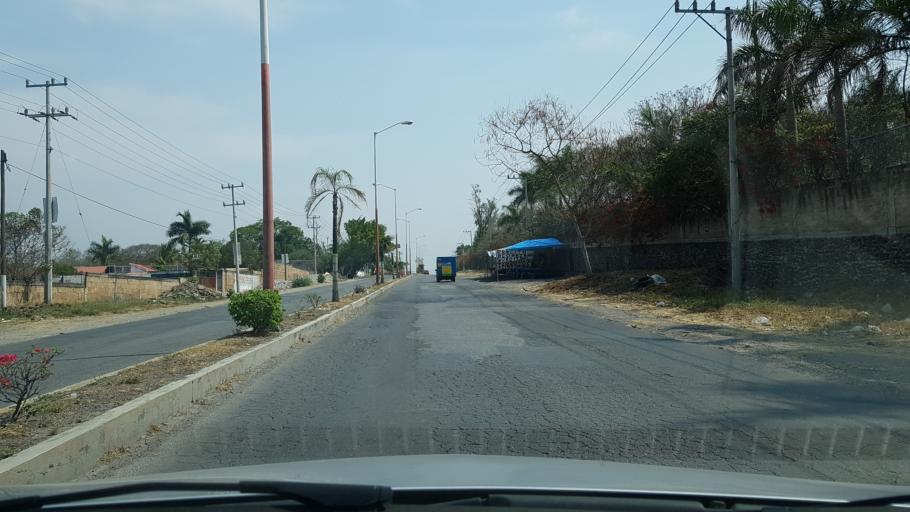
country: MX
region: Morelos
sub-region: Xochitepec
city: Chiconcuac
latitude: 18.7911
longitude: -99.2028
